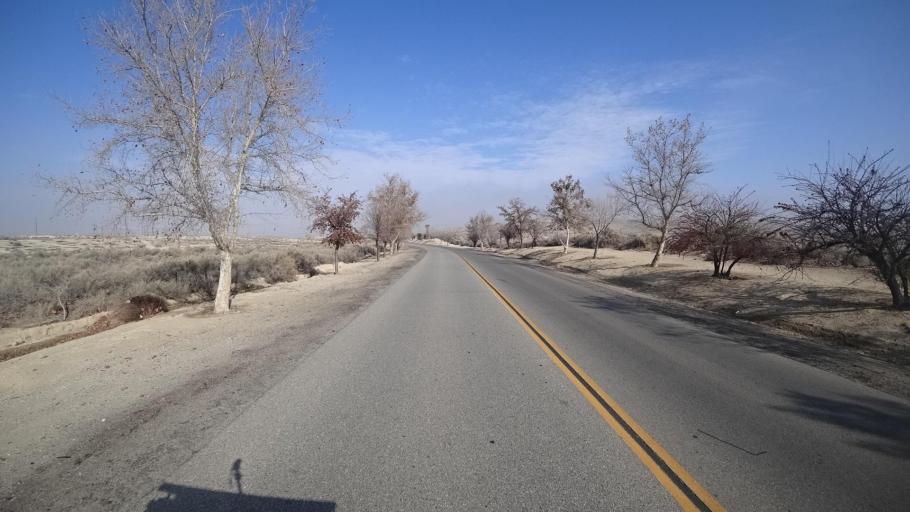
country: US
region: California
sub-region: Kern County
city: Ford City
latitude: 35.1624
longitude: -119.4556
